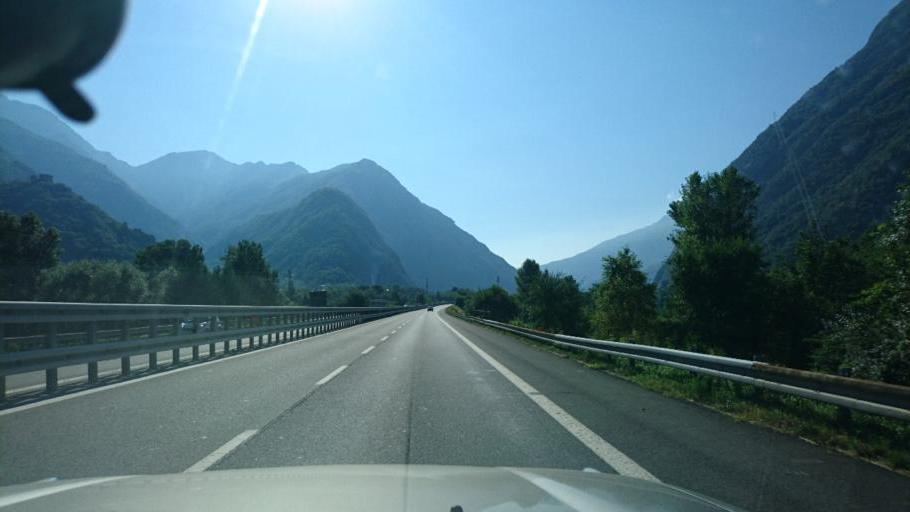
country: IT
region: Aosta Valley
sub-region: Valle d'Aosta
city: Arnad
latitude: 45.6440
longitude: 7.7148
